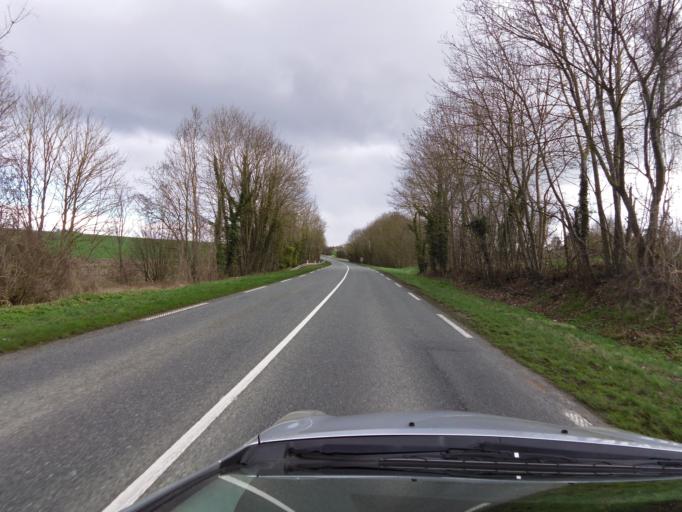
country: FR
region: Picardie
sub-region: Departement de l'Oise
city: Remy
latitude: 49.4985
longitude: 2.6774
